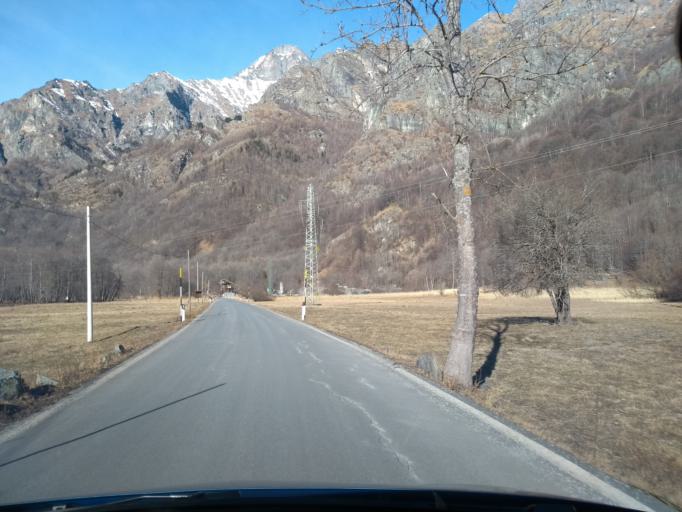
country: IT
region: Piedmont
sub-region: Provincia di Torino
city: Usseglio
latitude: 45.2284
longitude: 7.2470
